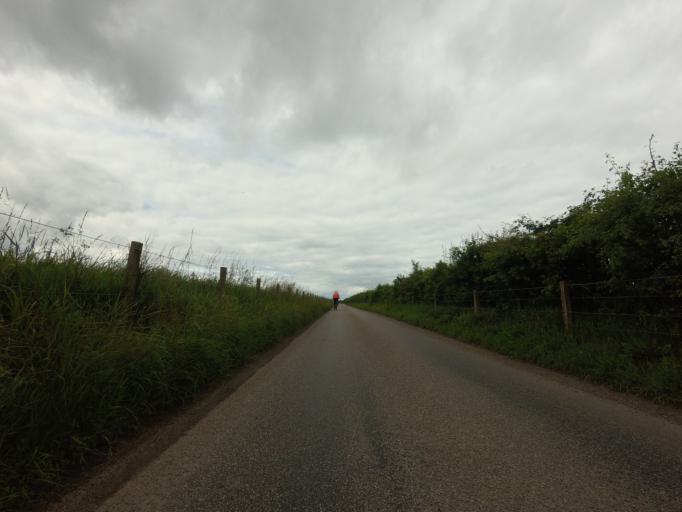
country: GB
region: Scotland
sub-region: Moray
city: Forres
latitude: 57.6214
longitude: -3.6643
